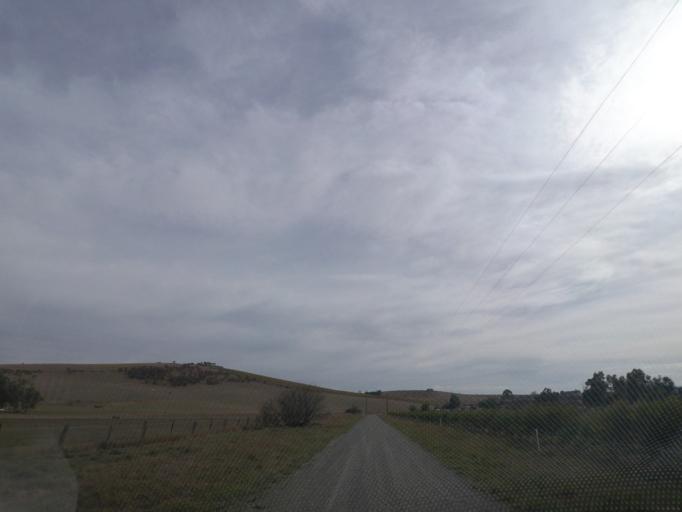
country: AU
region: Victoria
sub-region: Yarra Ranges
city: Yarra Glen
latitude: -37.6540
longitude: 145.4222
